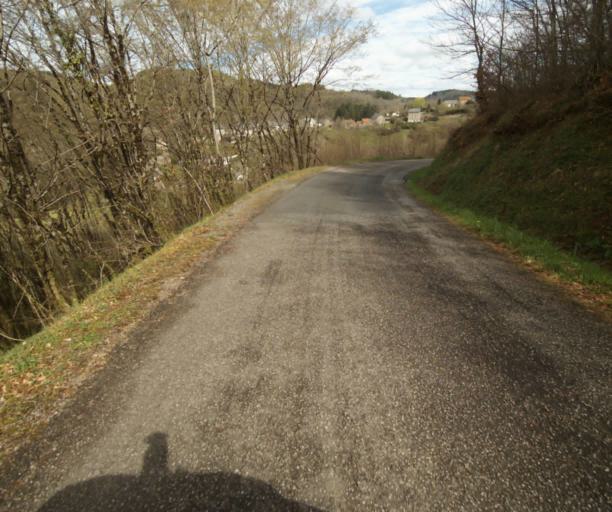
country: FR
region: Limousin
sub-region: Departement de la Correze
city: Laguenne
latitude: 45.2525
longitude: 1.8331
